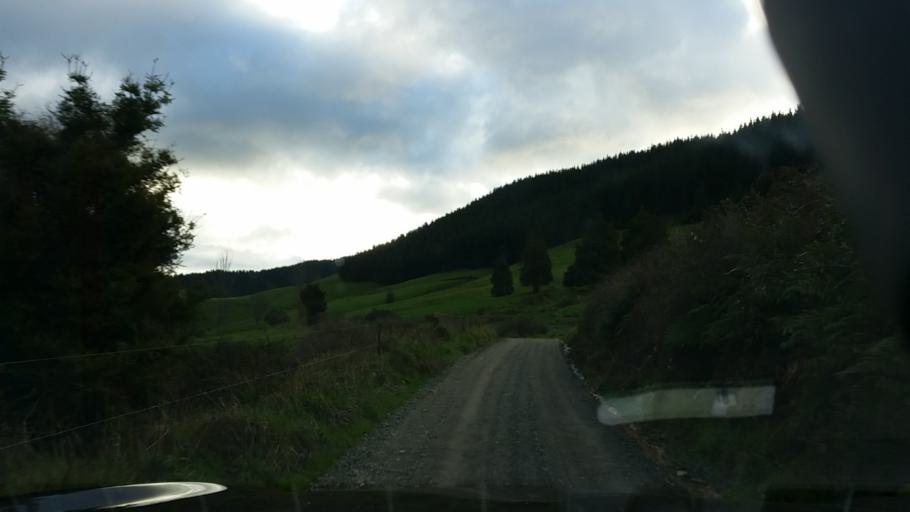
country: NZ
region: Nelson
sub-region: Nelson City
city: Nelson
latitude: -41.2083
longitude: 173.6411
